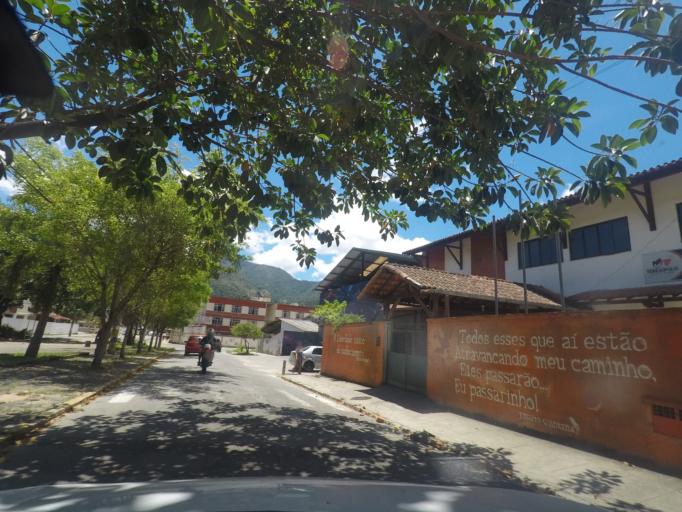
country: BR
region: Rio de Janeiro
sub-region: Teresopolis
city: Teresopolis
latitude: -22.4338
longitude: -42.9702
